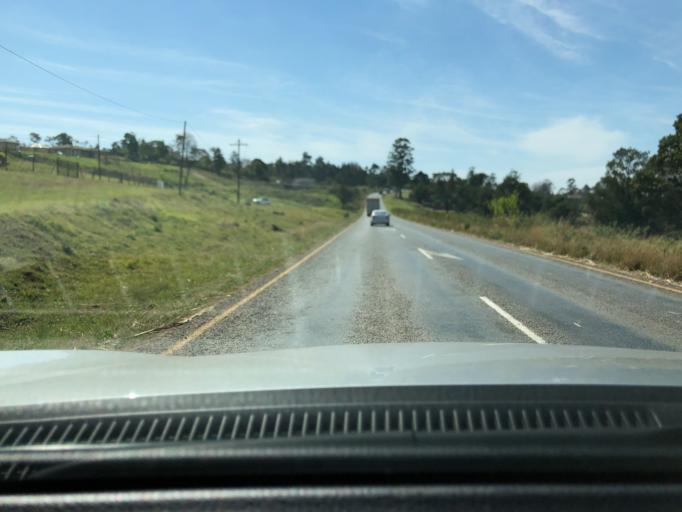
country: ZA
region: KwaZulu-Natal
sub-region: uMgungundlovu District Municipality
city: Camperdown
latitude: -29.7371
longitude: 30.4289
